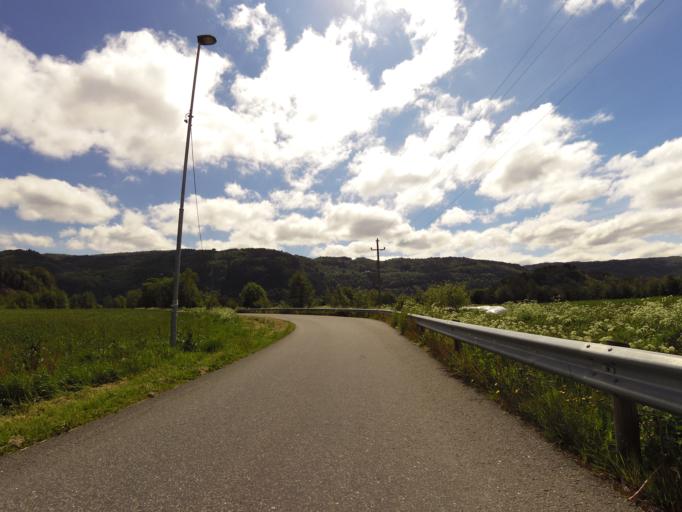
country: NO
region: Vest-Agder
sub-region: Kvinesdal
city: Liknes
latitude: 58.3067
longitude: 6.9367
